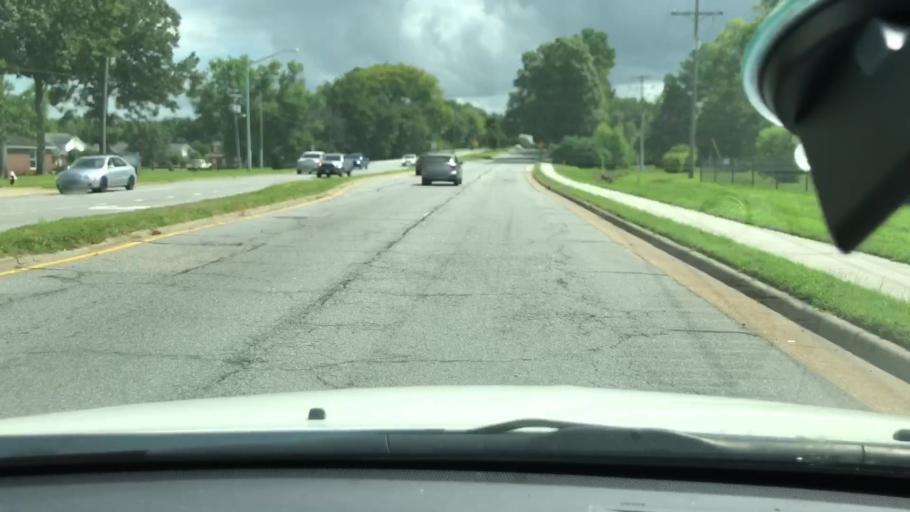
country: US
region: Virginia
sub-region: City of Chesapeake
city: Chesapeake
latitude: 36.8128
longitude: -76.1991
